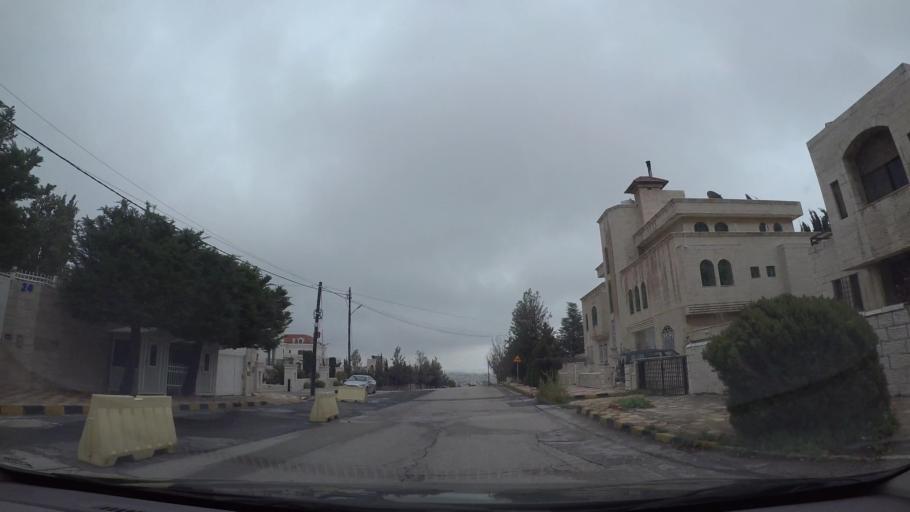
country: JO
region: Amman
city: Al Bunayyat ash Shamaliyah
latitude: 31.9377
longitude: 35.8833
